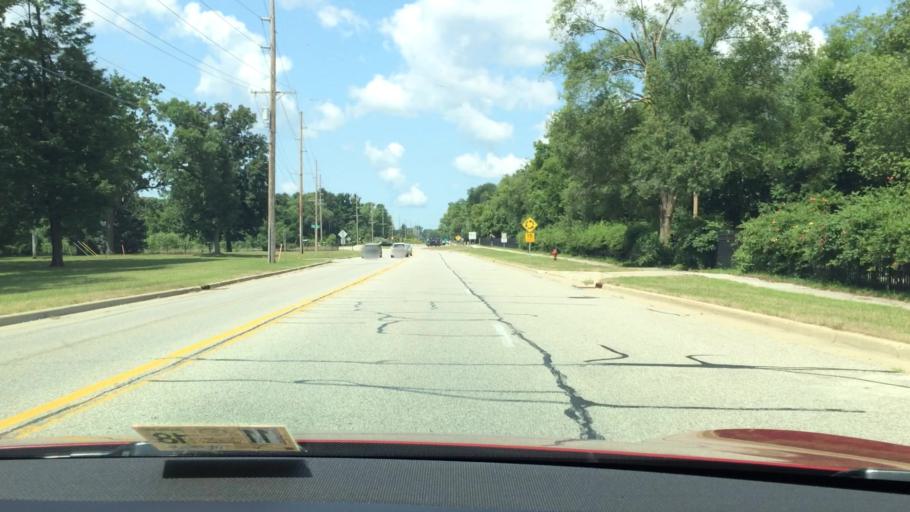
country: US
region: Indiana
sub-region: Saint Joseph County
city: Notre Dame
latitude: 41.7090
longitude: -86.2246
